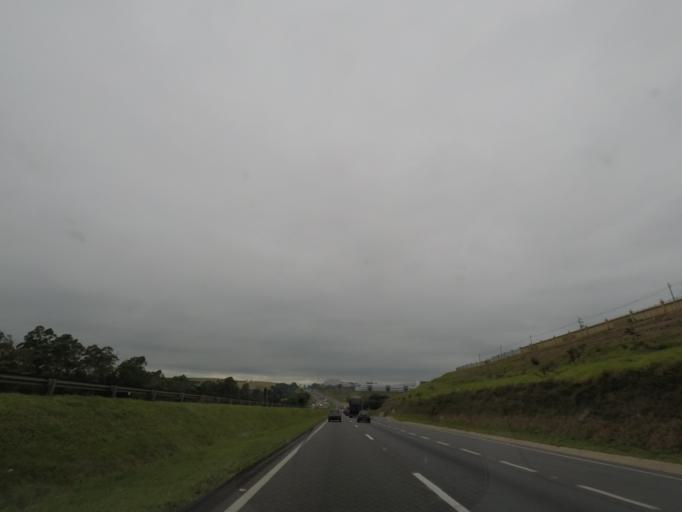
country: BR
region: Sao Paulo
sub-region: Jarinu
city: Jarinu
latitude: -23.0365
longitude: -46.7091
